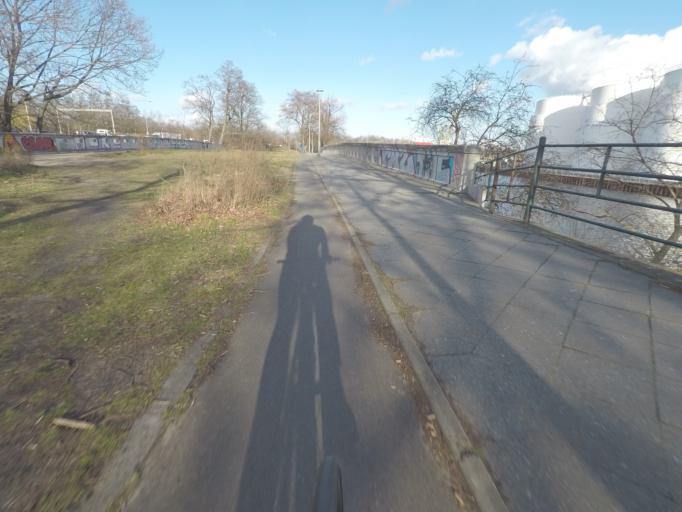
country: DE
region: Berlin
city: Moabit
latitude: 52.5386
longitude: 13.3296
